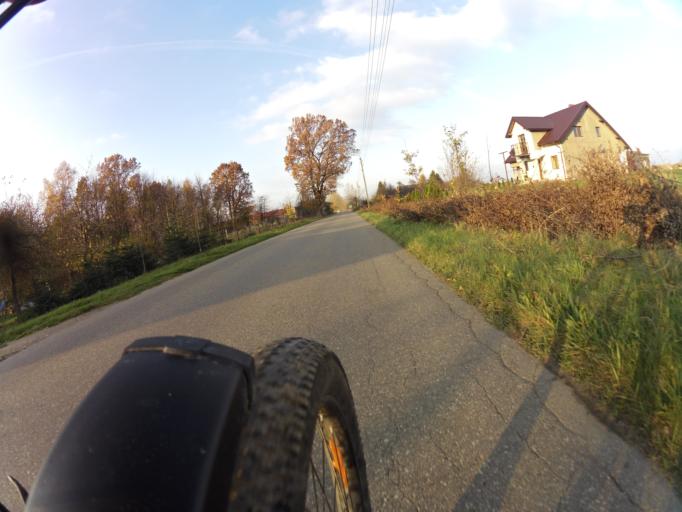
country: PL
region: Pomeranian Voivodeship
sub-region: Powiat pucki
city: Krokowa
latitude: 54.7667
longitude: 18.1803
